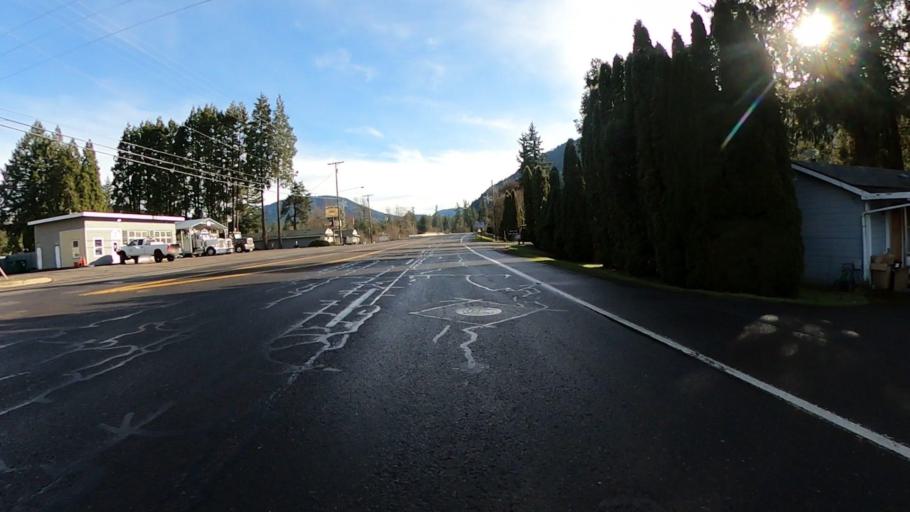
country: US
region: Oregon
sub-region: Lane County
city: Oakridge
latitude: 43.7418
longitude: -122.4608
